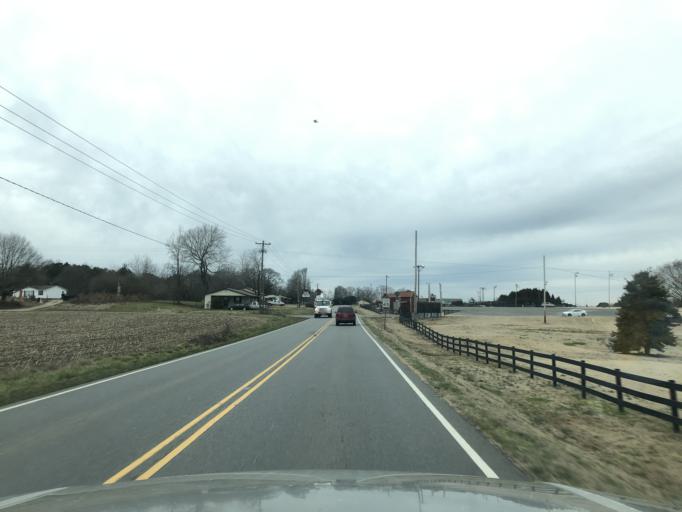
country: US
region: North Carolina
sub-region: Cleveland County
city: Shelby
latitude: 35.3358
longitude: -81.5020
